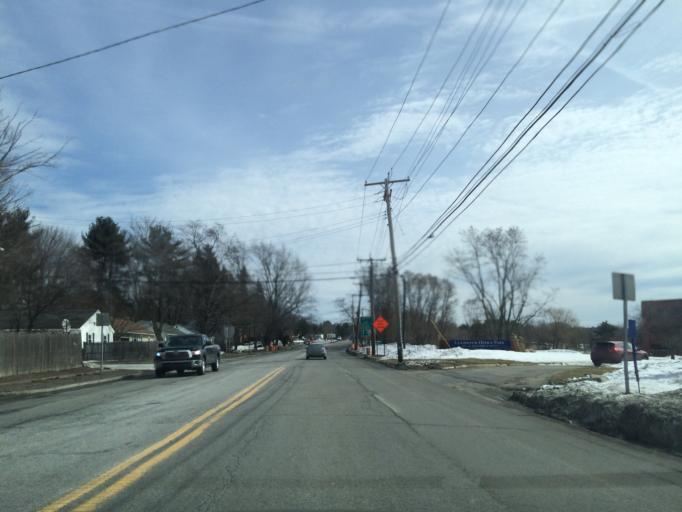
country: US
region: Massachusetts
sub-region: Middlesex County
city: Bedford
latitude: 42.4738
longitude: -71.2483
